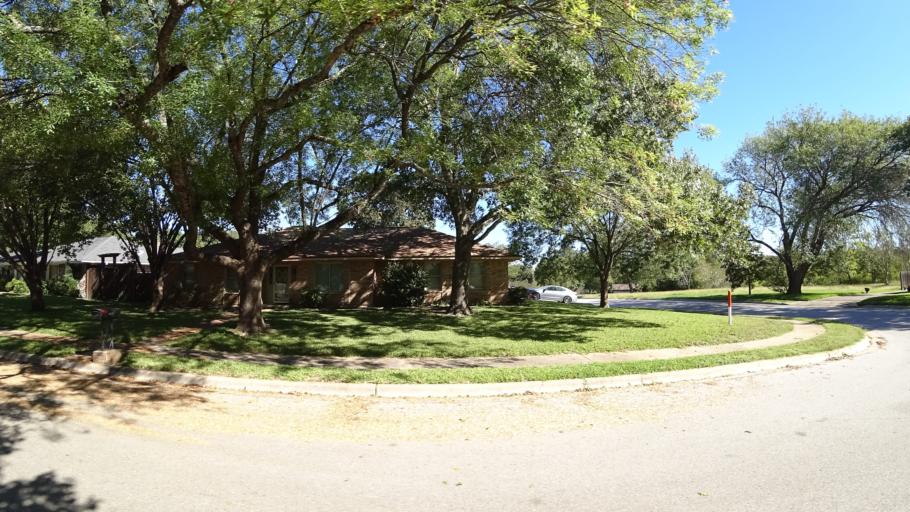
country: US
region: Texas
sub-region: Travis County
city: Manor
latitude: 30.3319
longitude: -97.6518
